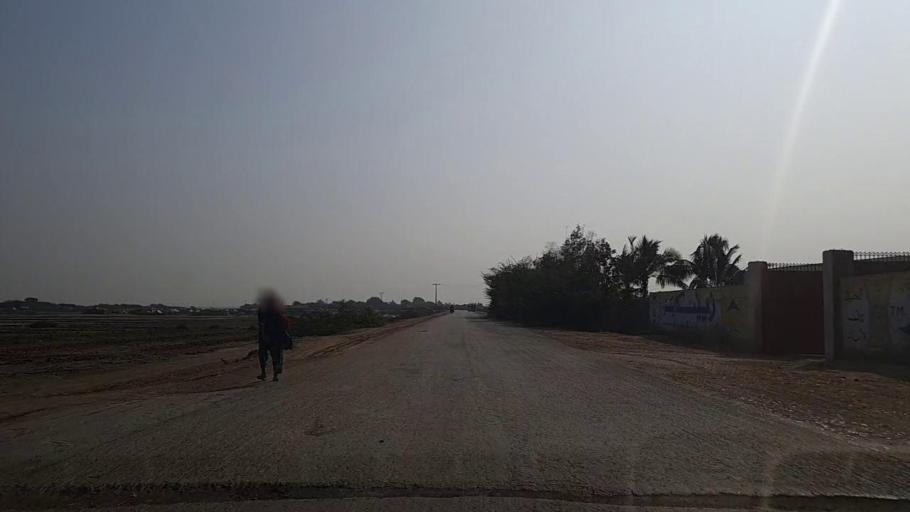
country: PK
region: Sindh
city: Keti Bandar
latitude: 24.2353
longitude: 67.6079
